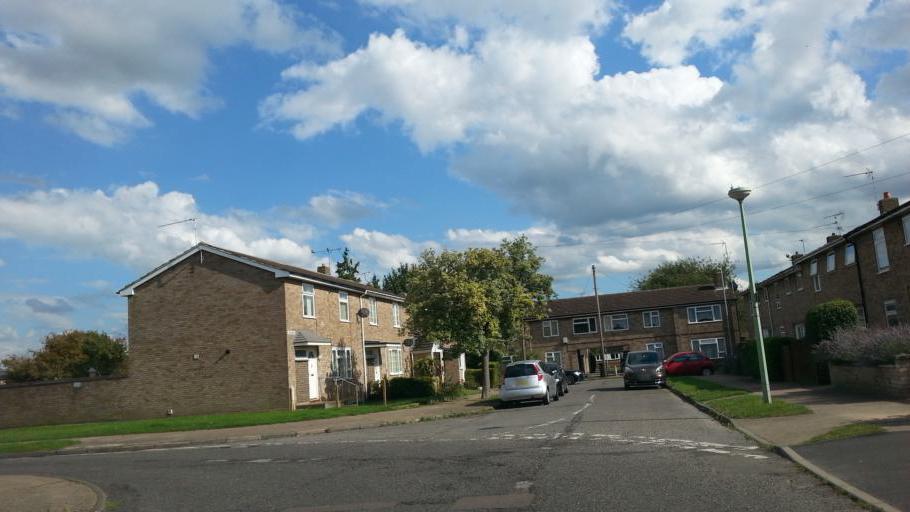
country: GB
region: England
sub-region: Suffolk
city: Bury St Edmunds
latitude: 52.2612
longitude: 0.6964
